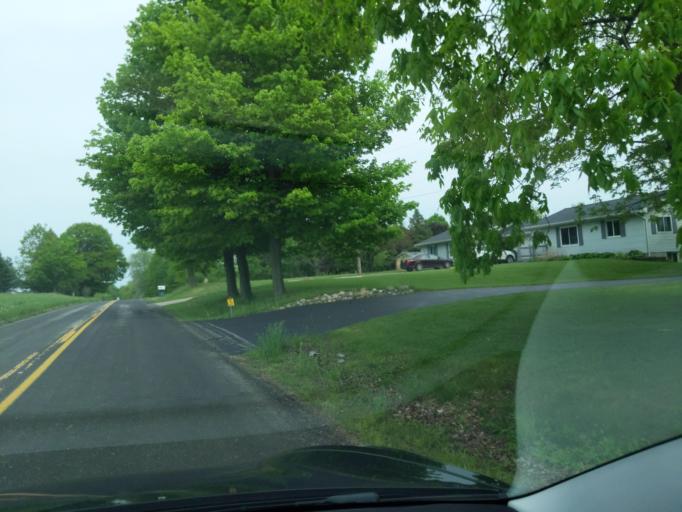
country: US
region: Michigan
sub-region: Ingham County
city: Leslie
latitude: 42.4657
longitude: -84.4299
